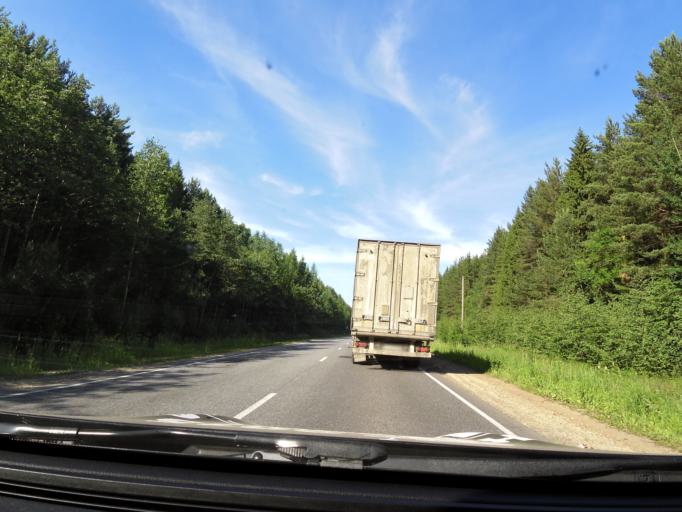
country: RU
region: Kirov
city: Belaya Kholunitsa
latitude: 58.8759
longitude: 50.8636
